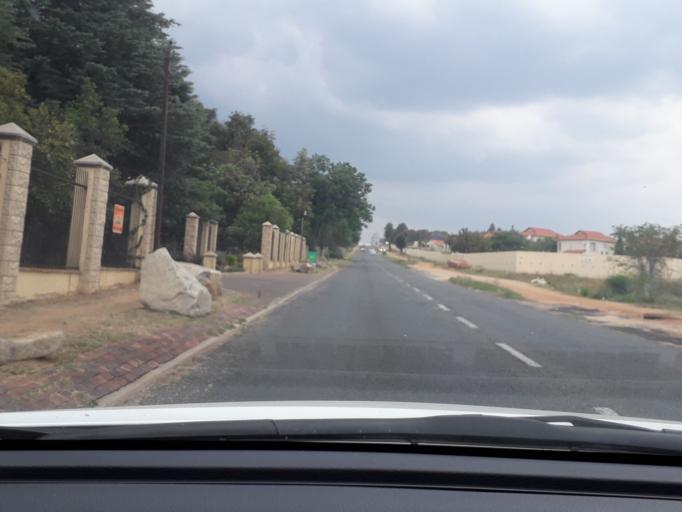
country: ZA
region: Gauteng
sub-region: West Rand District Municipality
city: Muldersdriseloop
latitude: -26.0652
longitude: 27.9250
